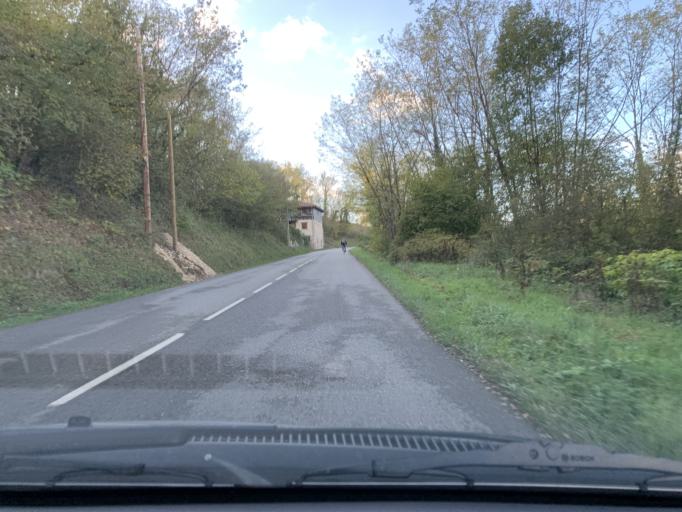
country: FR
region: Rhone-Alpes
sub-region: Departement de la Drome
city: Saint-Jean-en-Royans
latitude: 45.0288
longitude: 5.3090
